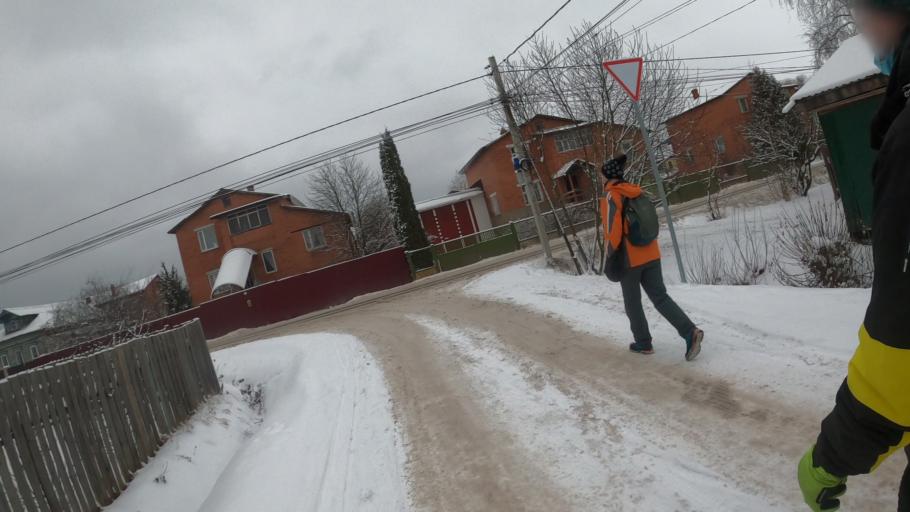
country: RU
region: Jaroslavl
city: Pereslavl'-Zalesskiy
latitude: 56.7268
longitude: 38.8357
